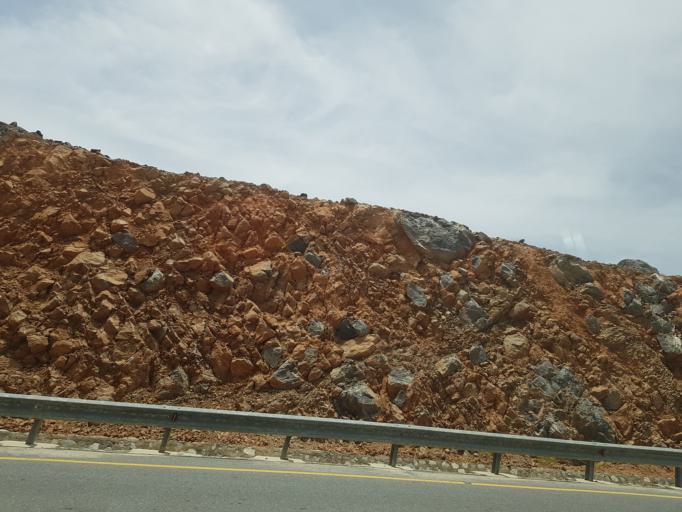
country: OM
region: Muhafazat ad Dakhiliyah
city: Izki
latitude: 22.9752
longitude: 57.6992
